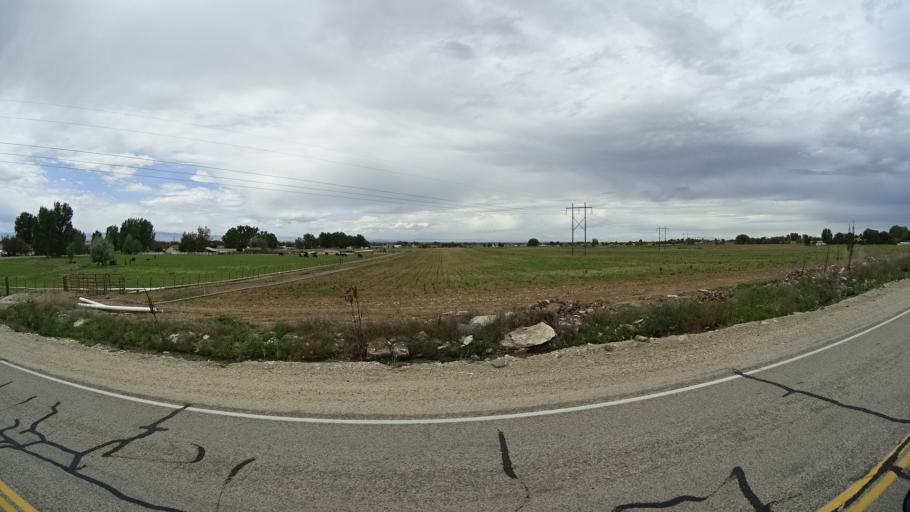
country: US
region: Idaho
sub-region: Ada County
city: Kuna
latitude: 43.5480
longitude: -116.4139
